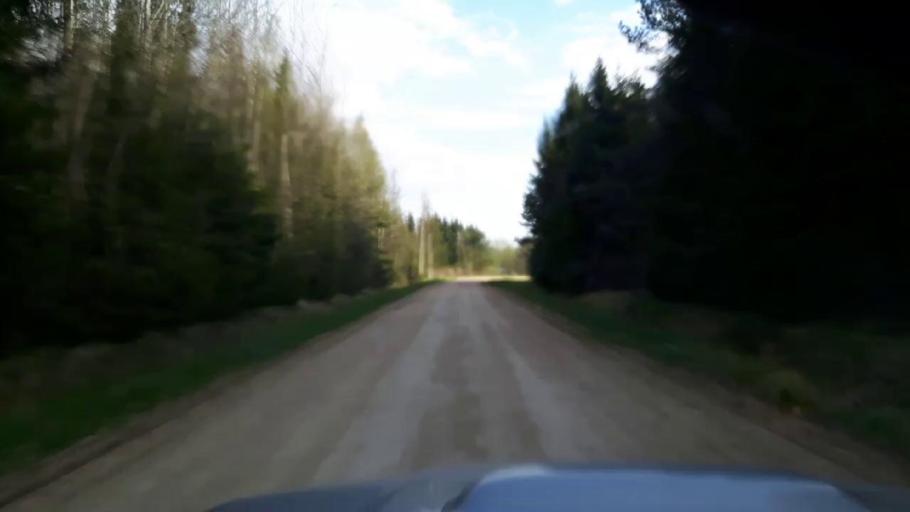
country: EE
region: Paernumaa
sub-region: Tootsi vald
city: Tootsi
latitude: 58.4483
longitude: 24.8214
